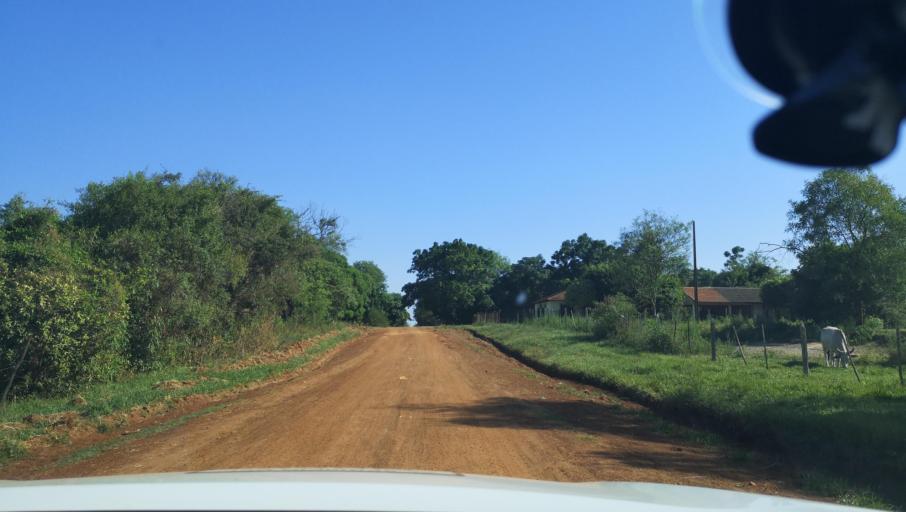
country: PY
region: Itapua
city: Carmen del Parana
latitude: -27.1693
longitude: -56.2370
